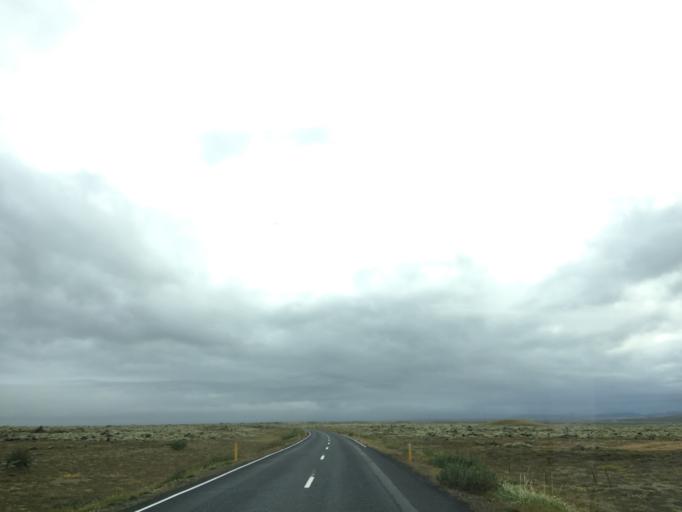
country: IS
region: South
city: Vestmannaeyjar
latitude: 63.6683
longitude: -18.4073
